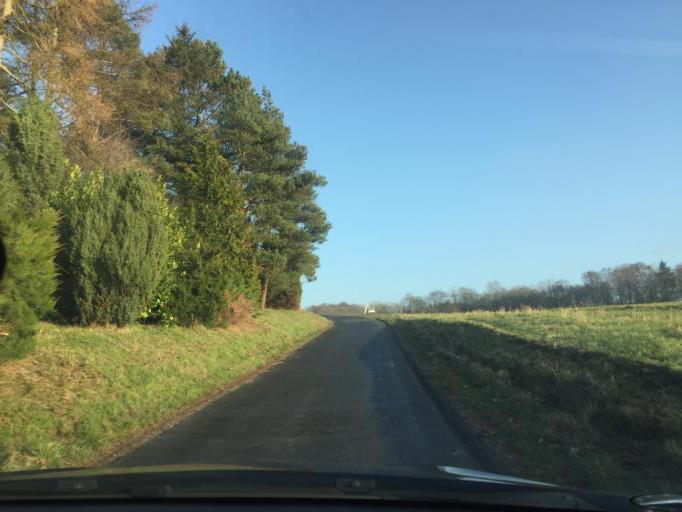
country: DK
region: South Denmark
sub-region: Faaborg-Midtfyn Kommune
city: Faaborg
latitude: 55.1310
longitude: 10.2442
